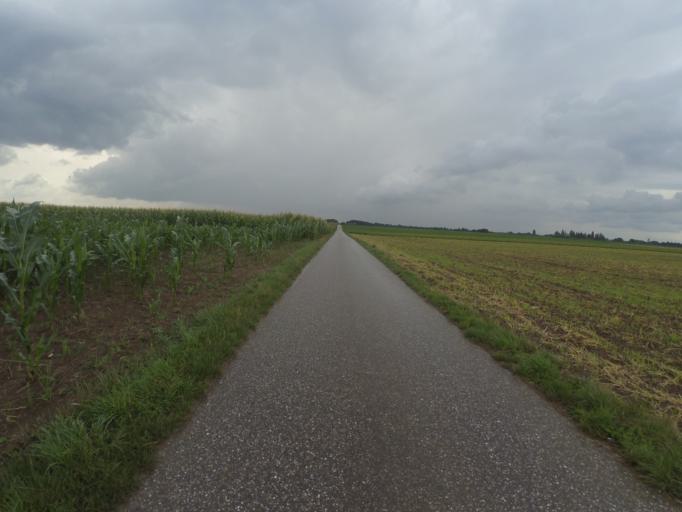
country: DE
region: North Rhine-Westphalia
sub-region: Regierungsbezirk Koln
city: Heinsberg
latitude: 51.0518
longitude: 6.0587
